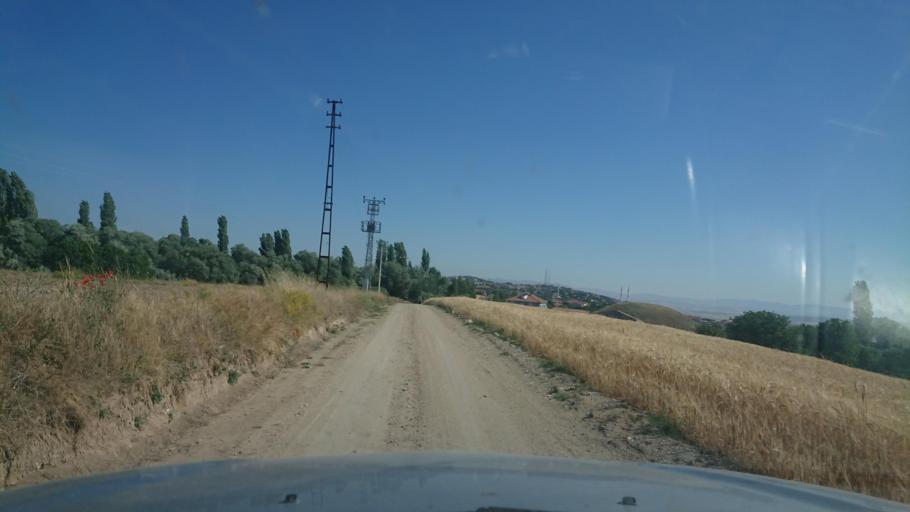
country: TR
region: Aksaray
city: Agacoren
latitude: 38.8601
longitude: 33.9121
